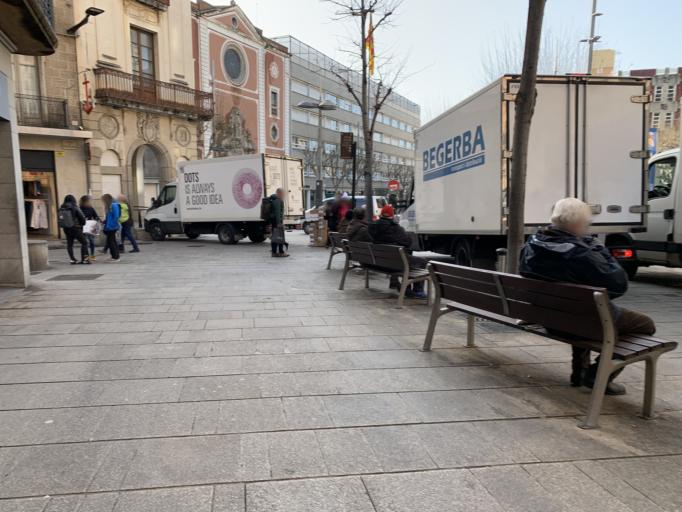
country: ES
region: Catalonia
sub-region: Provincia de Barcelona
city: Mataro
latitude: 41.5384
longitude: 2.4448
